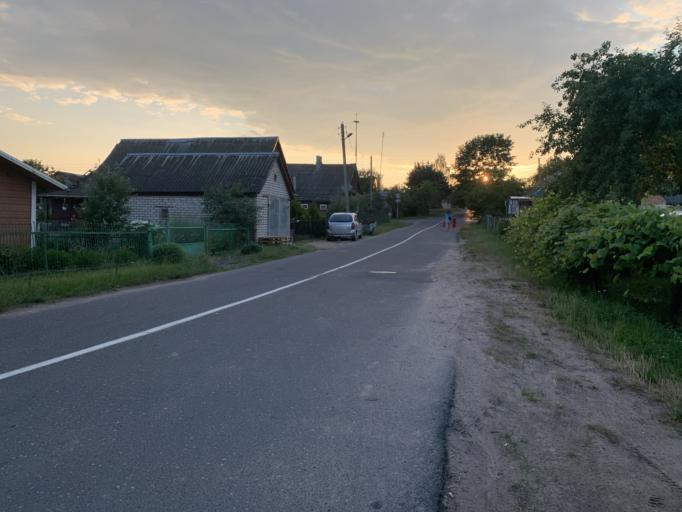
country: BY
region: Minsk
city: Nyasvizh
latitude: 53.2148
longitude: 26.6711
